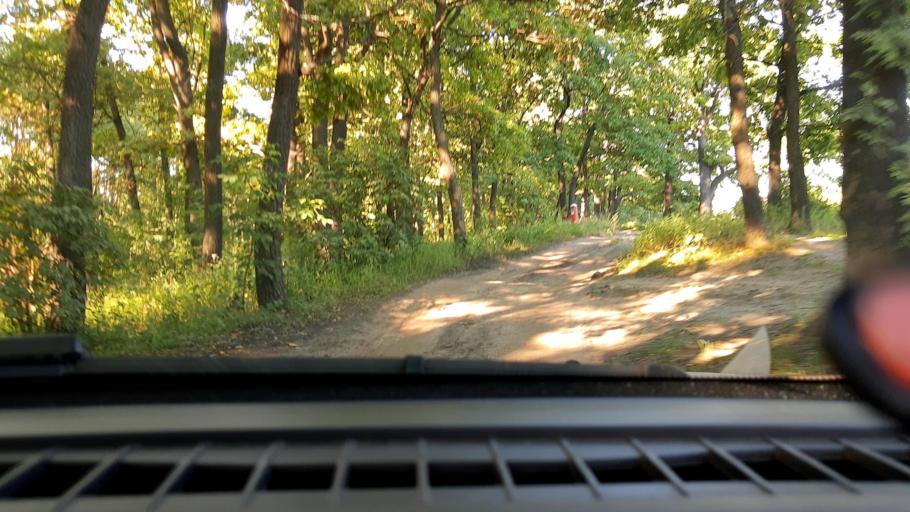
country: RU
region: Nizjnij Novgorod
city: Burevestnik
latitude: 56.2000
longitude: 43.8258
